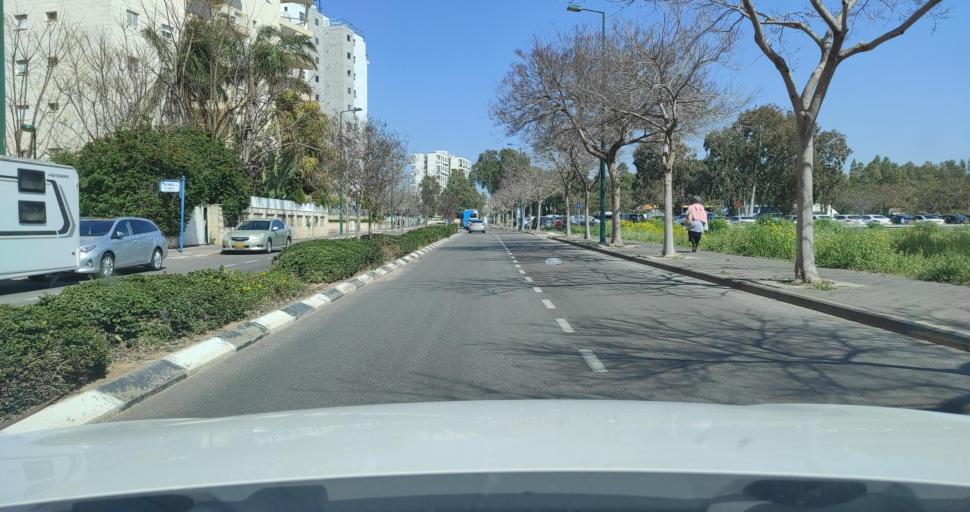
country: IL
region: Central District
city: Nordiyya
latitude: 32.3065
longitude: 34.8719
